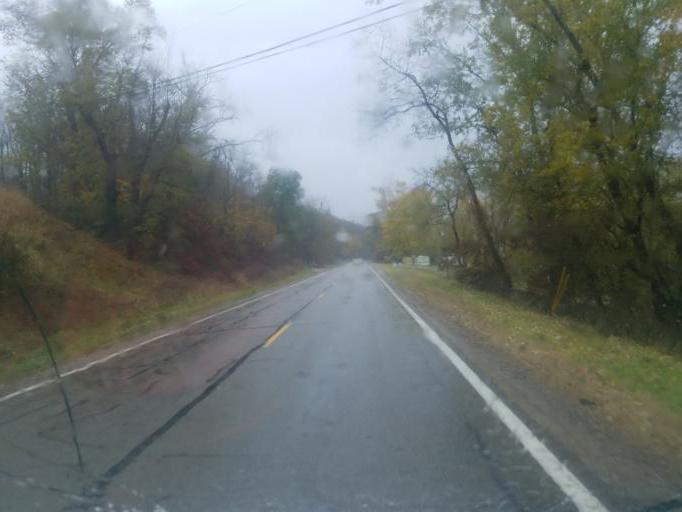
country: US
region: Ohio
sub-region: Muskingum County
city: South Zanesville
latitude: 39.8237
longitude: -81.8894
